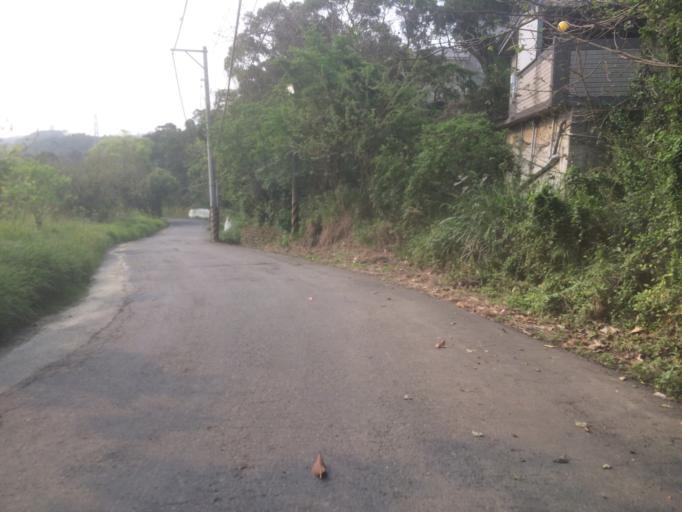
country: TW
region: Taiwan
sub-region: Hsinchu
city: Hsinchu
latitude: 24.7625
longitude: 120.9769
